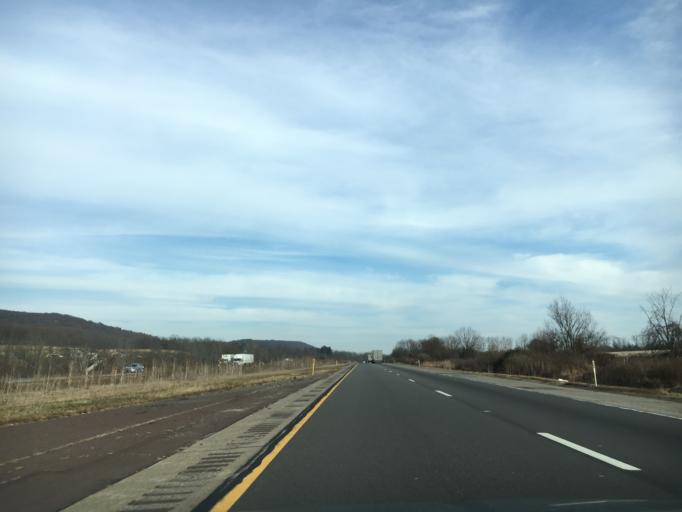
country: US
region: Pennsylvania
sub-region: Montour County
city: Mechanicsville
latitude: 41.0043
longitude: -76.5631
